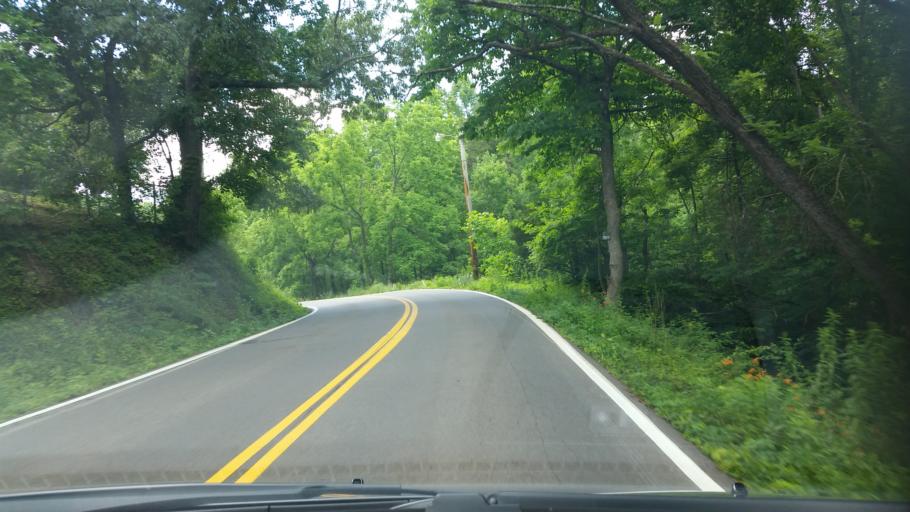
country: US
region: Tennessee
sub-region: Sevier County
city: Gatlinburg
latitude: 35.7506
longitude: -83.4353
